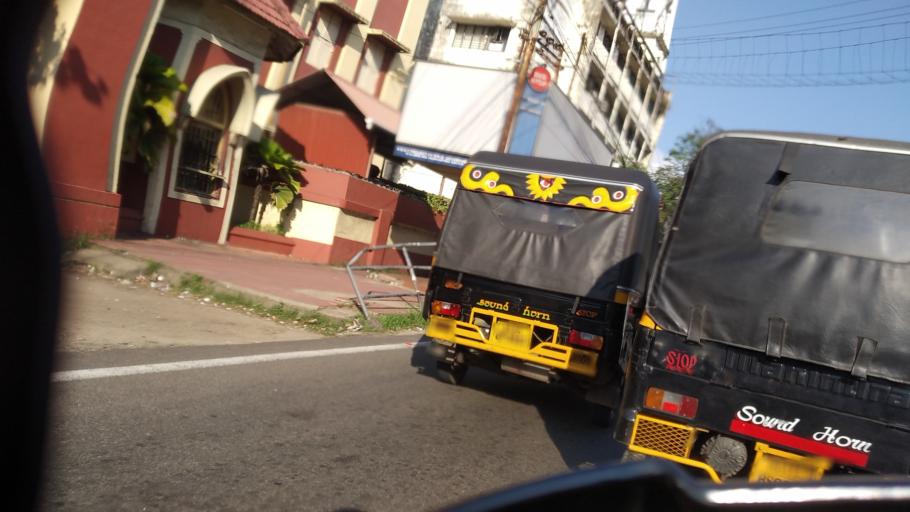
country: IN
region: Kerala
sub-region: Ernakulam
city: Cochin
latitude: 9.9855
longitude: 76.2788
